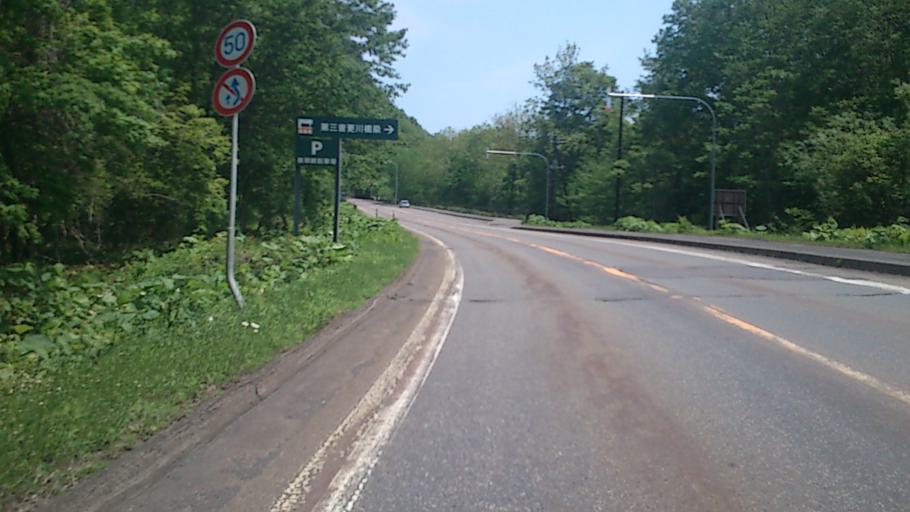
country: JP
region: Hokkaido
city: Otofuke
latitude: 43.3565
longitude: 143.2555
